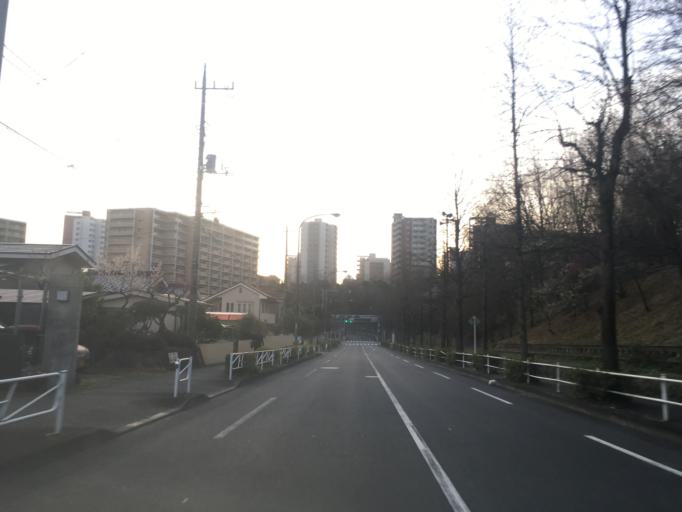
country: JP
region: Tokyo
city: Hino
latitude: 35.6207
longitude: 139.3750
